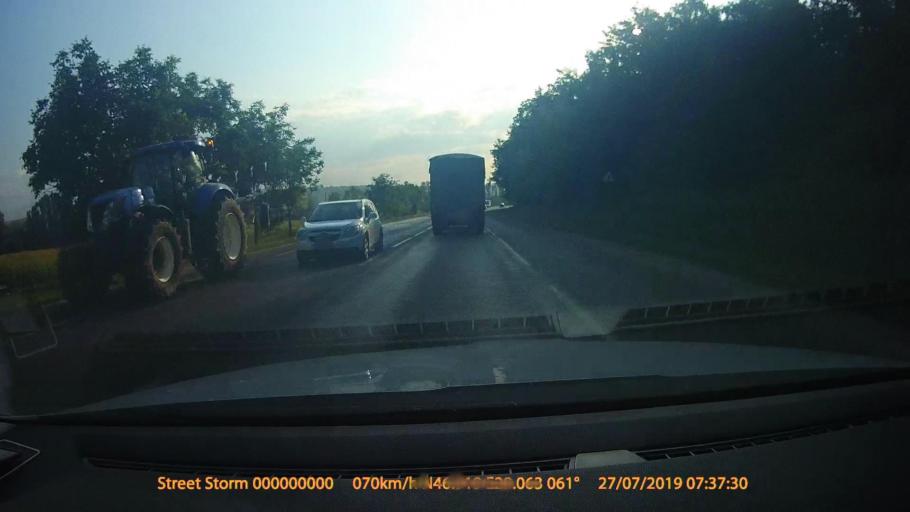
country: MD
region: Chisinau
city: Singera
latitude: 46.9188
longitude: 29.0618
